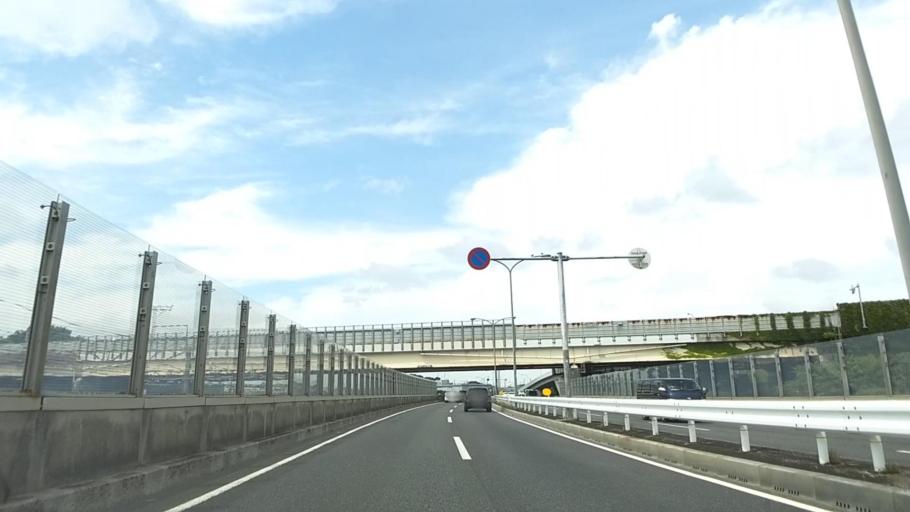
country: JP
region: Kanagawa
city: Yokohama
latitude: 35.4872
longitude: 139.5938
